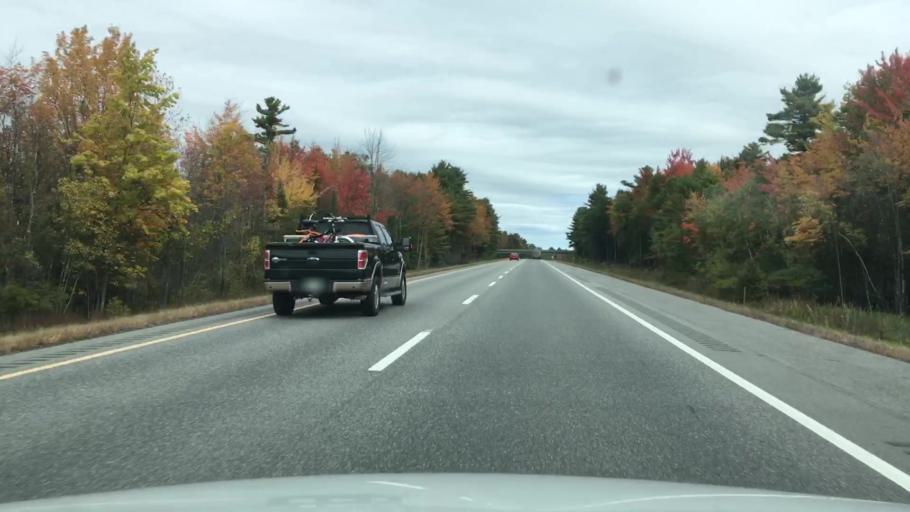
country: US
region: Maine
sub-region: Kennebec County
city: Sidney
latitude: 44.4187
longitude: -69.7424
